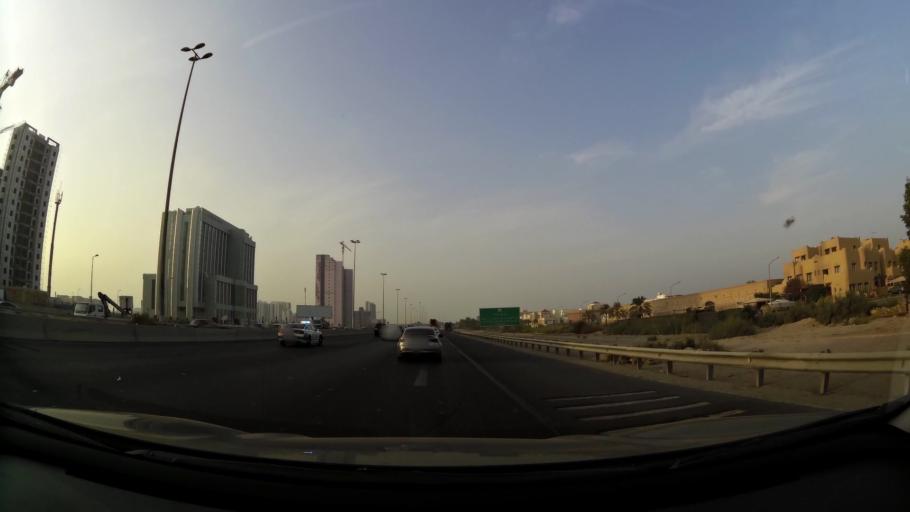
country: KW
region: Mubarak al Kabir
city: Sabah as Salim
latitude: 29.2566
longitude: 48.0892
